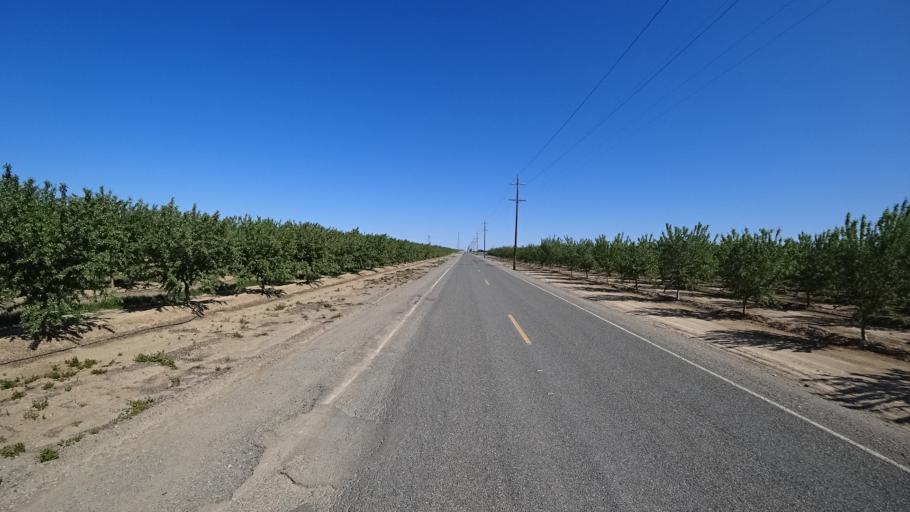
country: US
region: California
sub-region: Glenn County
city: Orland
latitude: 39.6440
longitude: -122.1786
